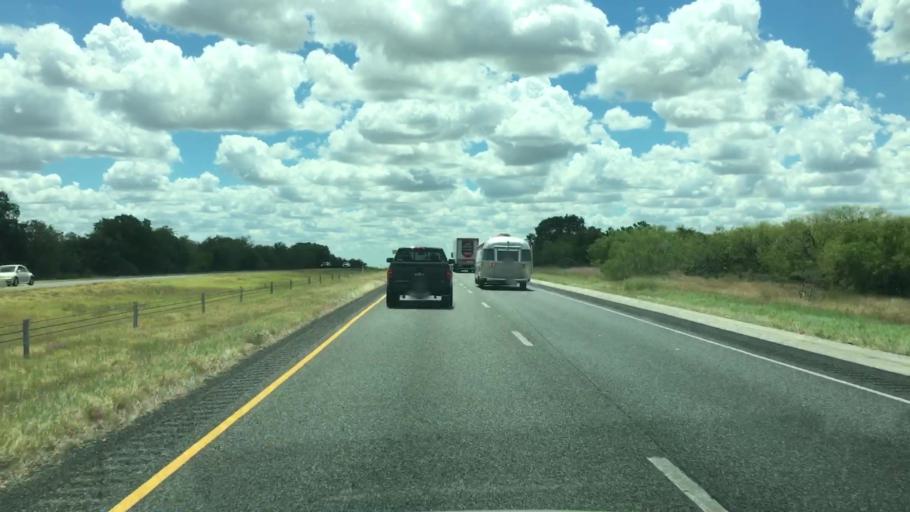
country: US
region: Texas
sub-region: Bexar County
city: Elmendorf
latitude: 29.1293
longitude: -98.4305
